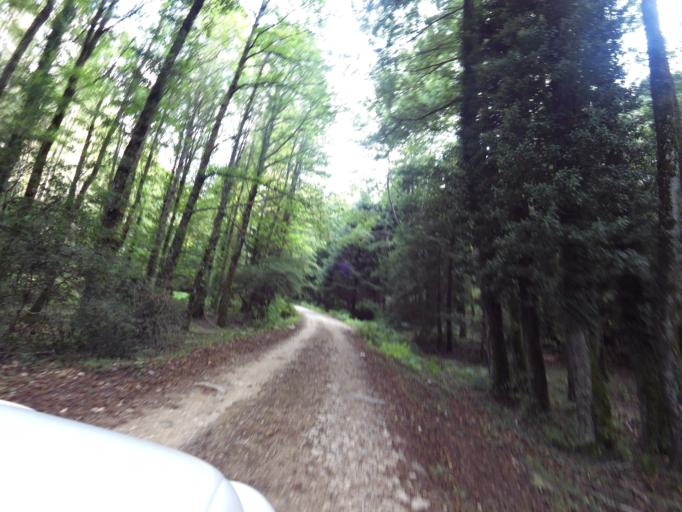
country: IT
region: Calabria
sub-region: Provincia di Vibo-Valentia
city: Nardodipace
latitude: 38.5138
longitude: 16.3787
